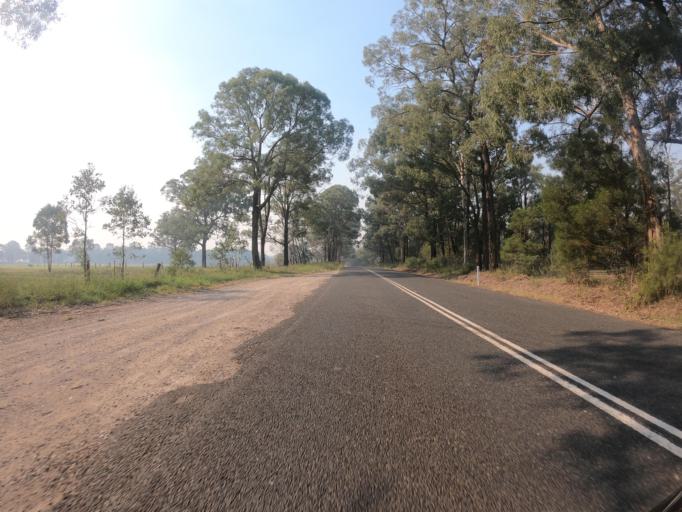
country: AU
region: New South Wales
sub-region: Wollondilly
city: Douglas Park
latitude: -34.2323
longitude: 150.7365
